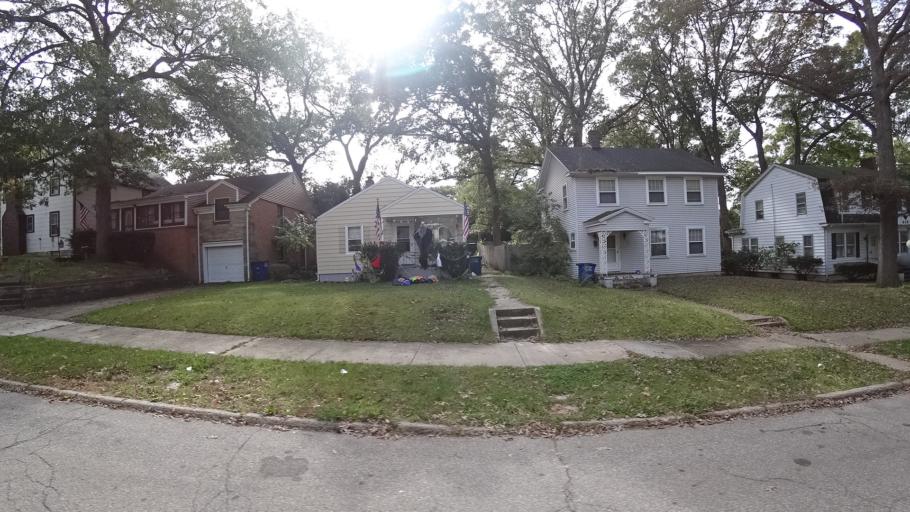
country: US
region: Indiana
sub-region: LaPorte County
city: Michigan City
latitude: 41.7143
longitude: -86.8807
